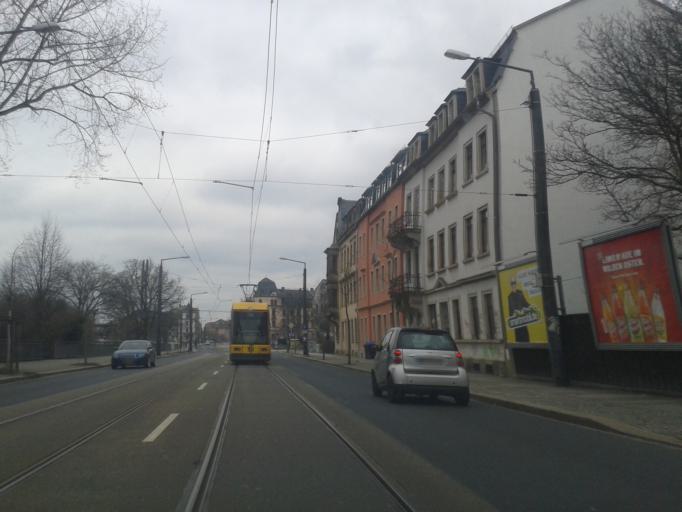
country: DE
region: Saxony
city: Dresden
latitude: 51.0755
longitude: 13.7214
